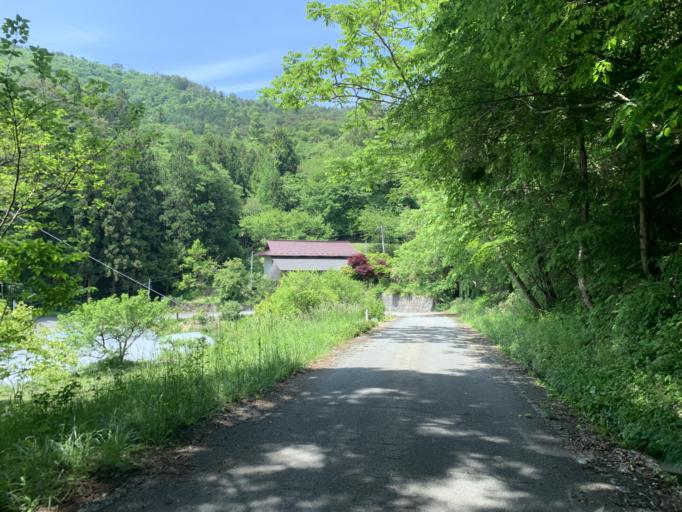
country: JP
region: Iwate
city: Ichinoseki
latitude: 38.9642
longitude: 141.2375
